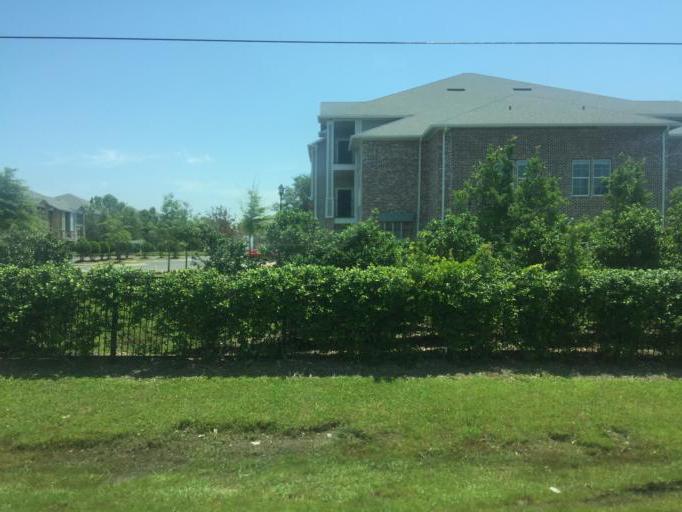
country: US
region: Florida
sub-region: Bay County
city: Lynn Haven
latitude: 30.2174
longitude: -85.6663
